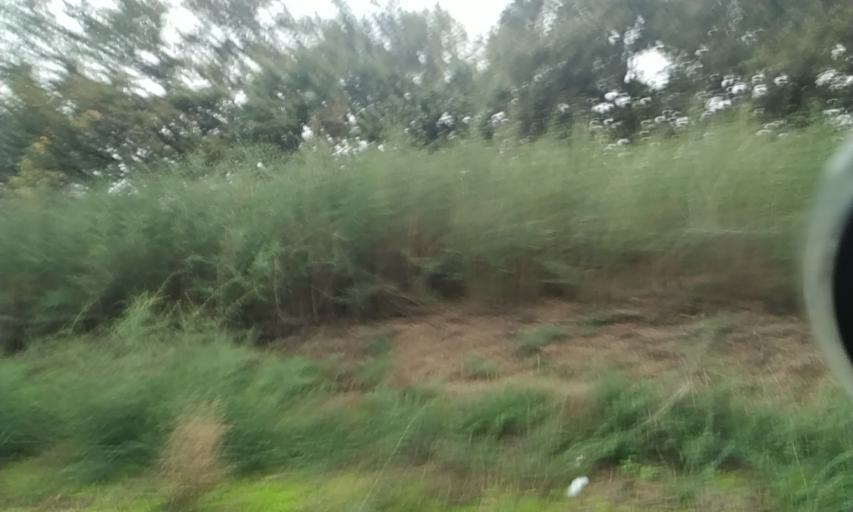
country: PT
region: Porto
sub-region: Amarante
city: Teloes
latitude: 41.2992
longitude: -8.0883
